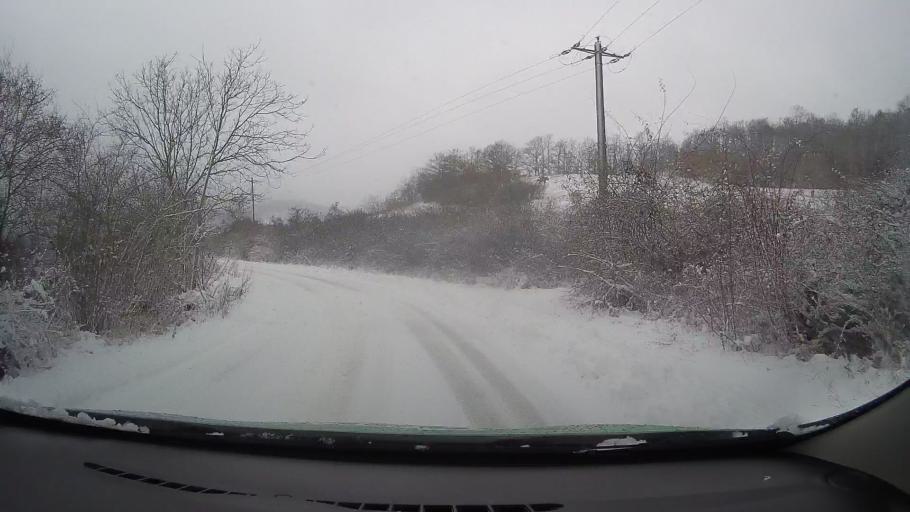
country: RO
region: Hunedoara
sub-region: Comuna Carjiti
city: Carjiti
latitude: 45.8395
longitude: 22.8406
